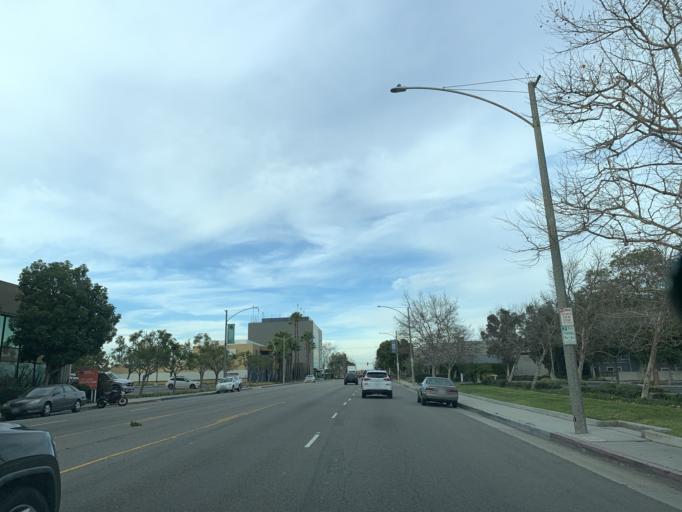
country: US
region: California
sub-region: Los Angeles County
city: Signal Hill
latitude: 33.8245
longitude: -118.1893
